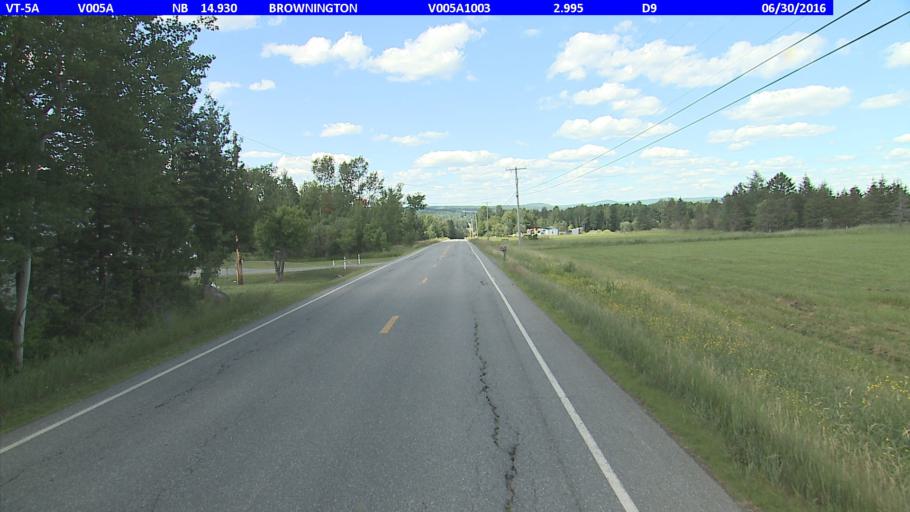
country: US
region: Vermont
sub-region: Orleans County
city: Newport
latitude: 44.8254
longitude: -72.0707
